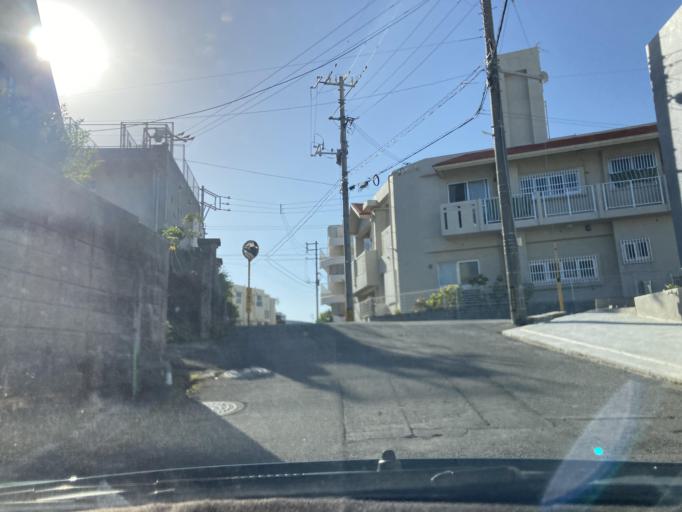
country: JP
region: Okinawa
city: Ginowan
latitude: 26.2382
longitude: 127.7263
